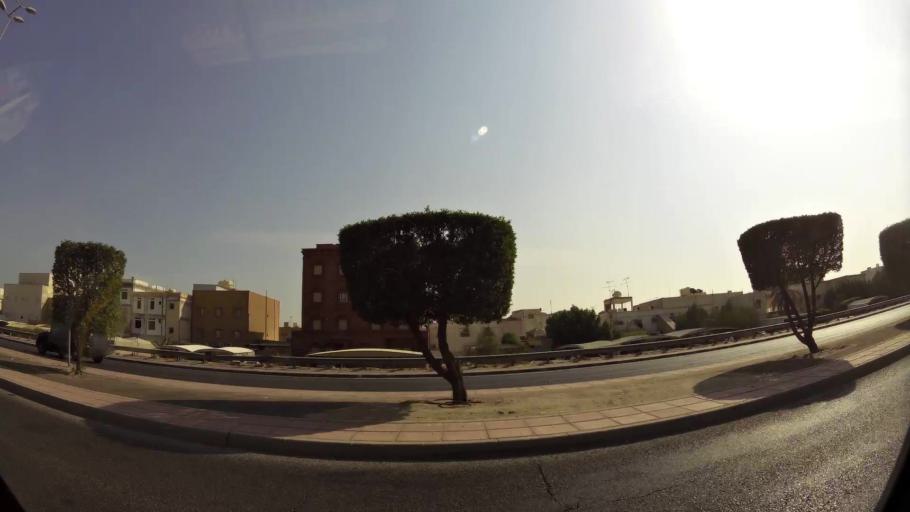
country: KW
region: Al Ahmadi
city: Ar Riqqah
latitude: 29.1597
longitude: 48.1043
